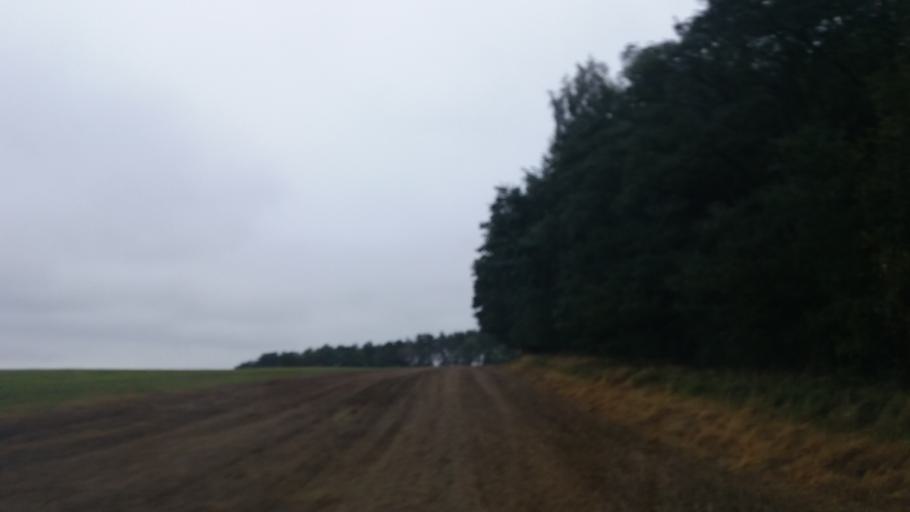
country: PL
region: West Pomeranian Voivodeship
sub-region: Powiat choszczenski
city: Pelczyce
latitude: 53.0702
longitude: 15.3035
